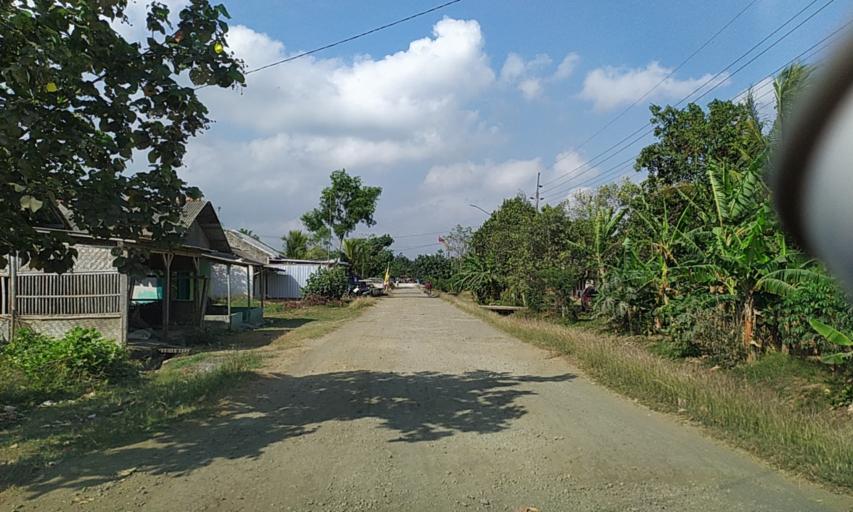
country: ID
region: Central Java
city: Sidakaya
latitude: -7.6180
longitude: 108.8581
